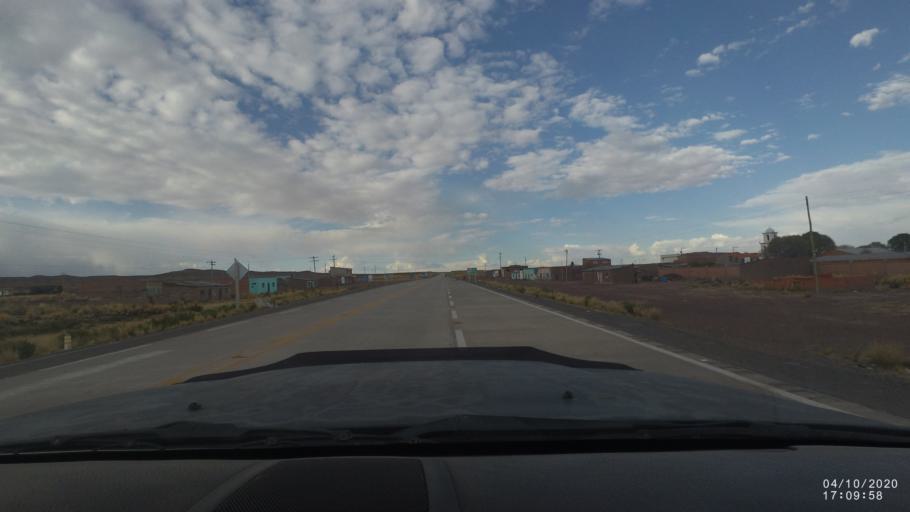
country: BO
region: Oruro
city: Oruro
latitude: -18.3361
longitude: -67.5876
